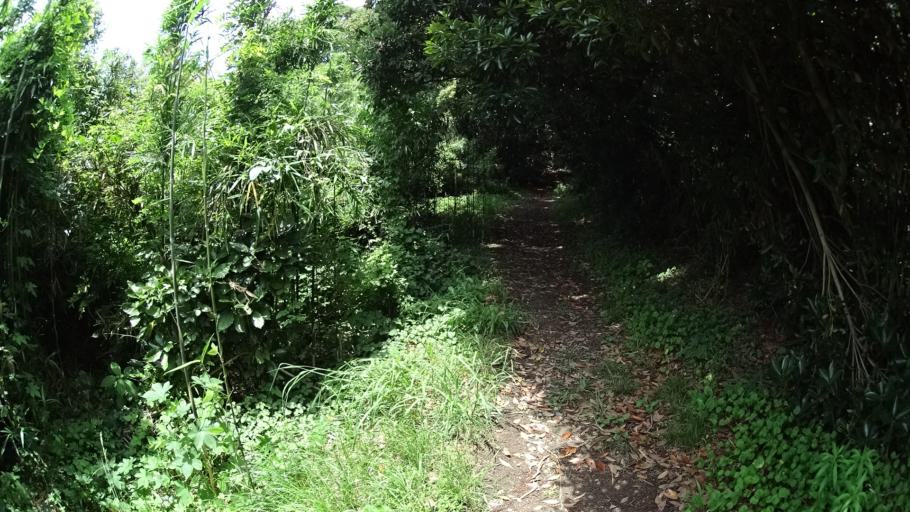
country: JP
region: Kanagawa
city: Yokosuka
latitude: 35.2071
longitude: 139.6710
